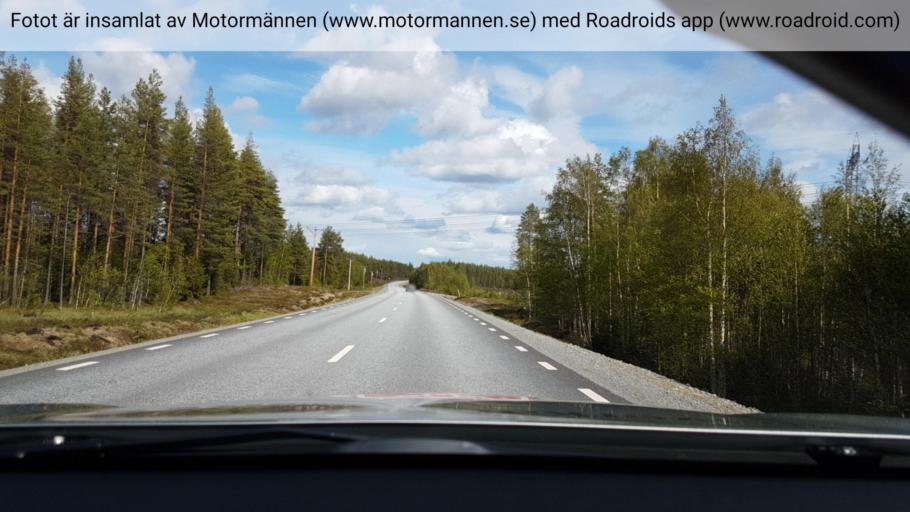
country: SE
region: Vaesternorrland
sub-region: OErnskoeldsviks Kommun
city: Bredbyn
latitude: 64.0818
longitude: 18.2621
